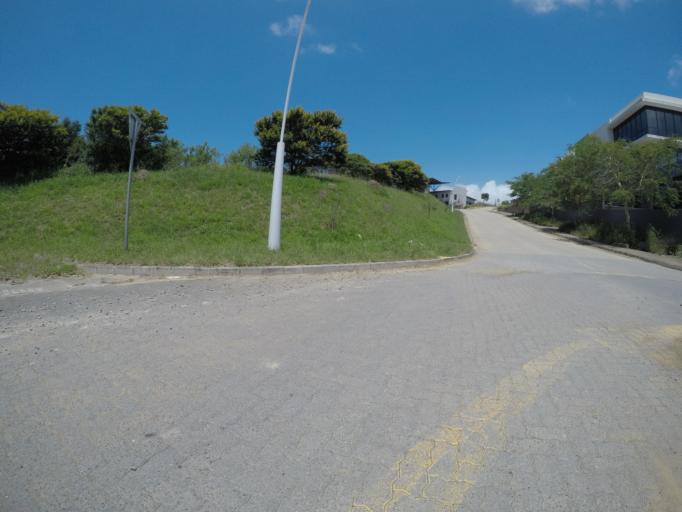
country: ZA
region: Eastern Cape
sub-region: Buffalo City Metropolitan Municipality
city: East London
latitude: -32.9472
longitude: 27.9417
